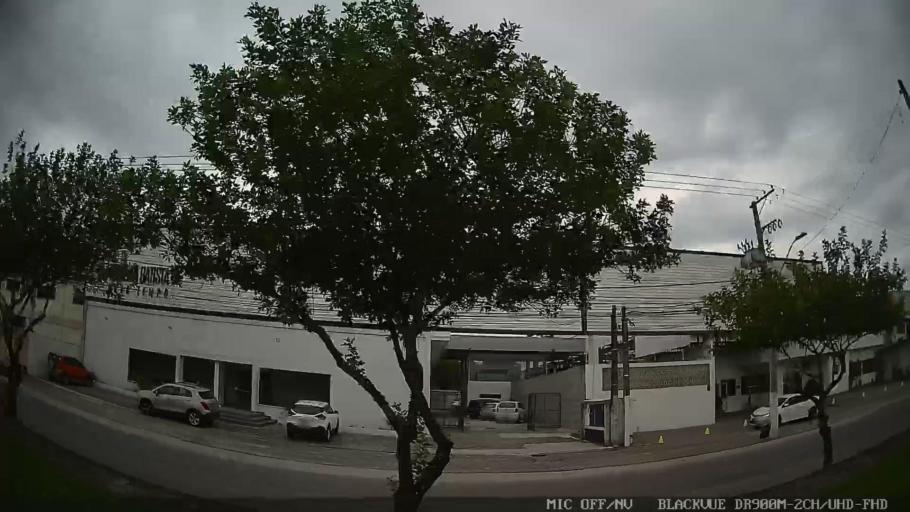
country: BR
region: Sao Paulo
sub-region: Caraguatatuba
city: Caraguatatuba
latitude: -23.6494
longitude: -45.4326
